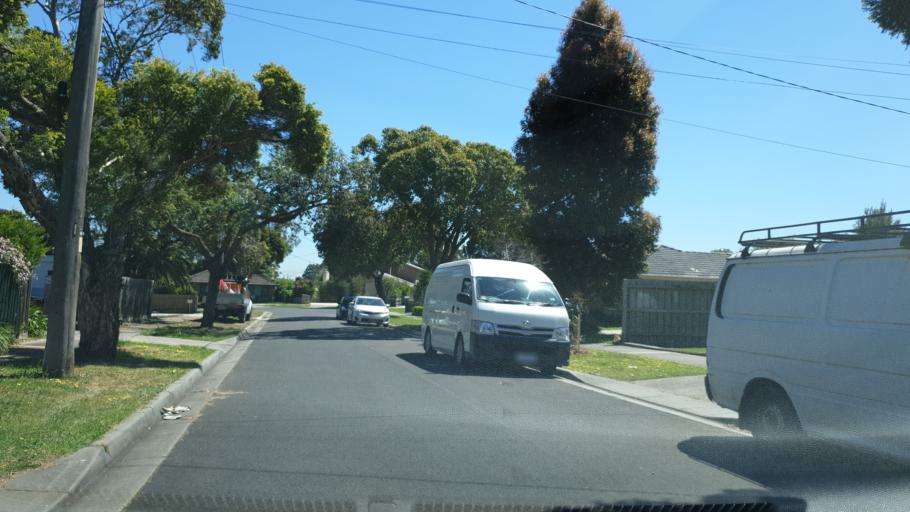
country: AU
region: Victoria
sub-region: Casey
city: Cranbourne
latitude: -38.0967
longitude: 145.2760
